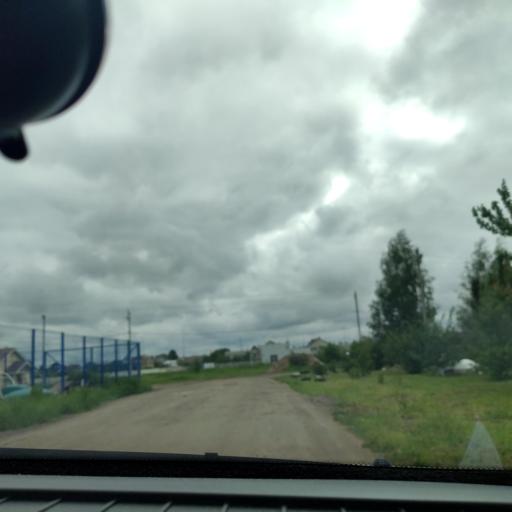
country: RU
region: Voronezj
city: Somovo
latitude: 51.6831
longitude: 39.3220
